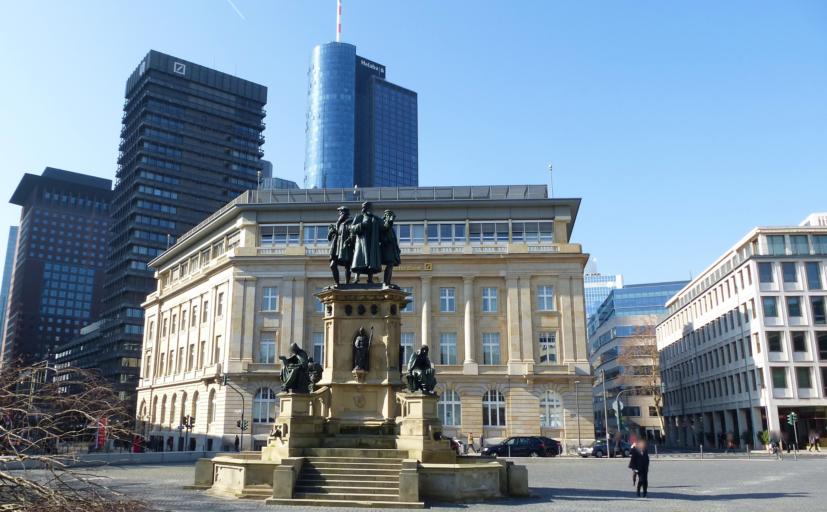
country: DE
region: Hesse
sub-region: Regierungsbezirk Darmstadt
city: Frankfurt am Main
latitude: 50.1124
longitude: 8.6771
